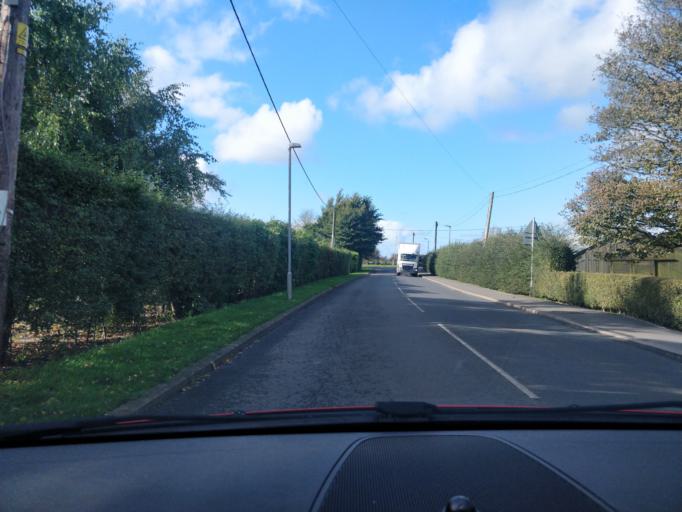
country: GB
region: England
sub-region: Lancashire
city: Banks
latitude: 53.6966
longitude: -2.8858
